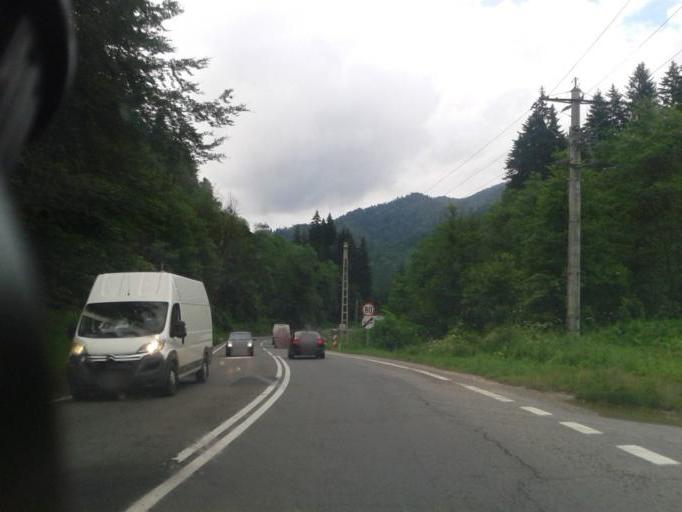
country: RO
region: Brasov
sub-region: Oras Predeal
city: Predeal
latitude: 45.5351
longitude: 25.5844
